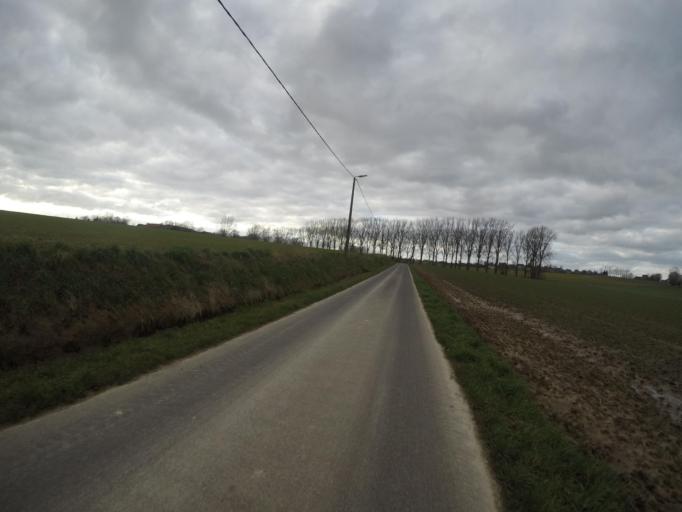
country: BE
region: Flanders
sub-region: Provincie Vlaams-Brabant
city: Pepingen
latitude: 50.7258
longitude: 4.1155
